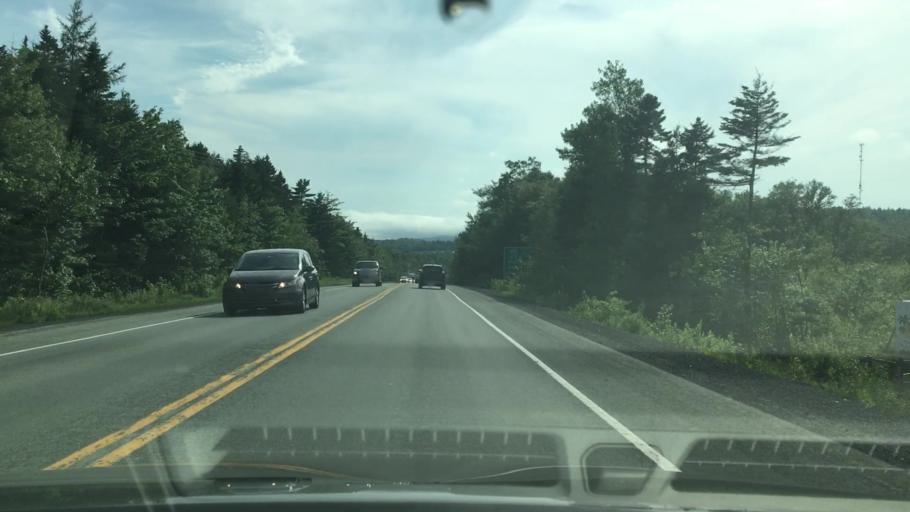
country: CA
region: Nova Scotia
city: Dartmouth
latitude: 44.7124
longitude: -63.8379
